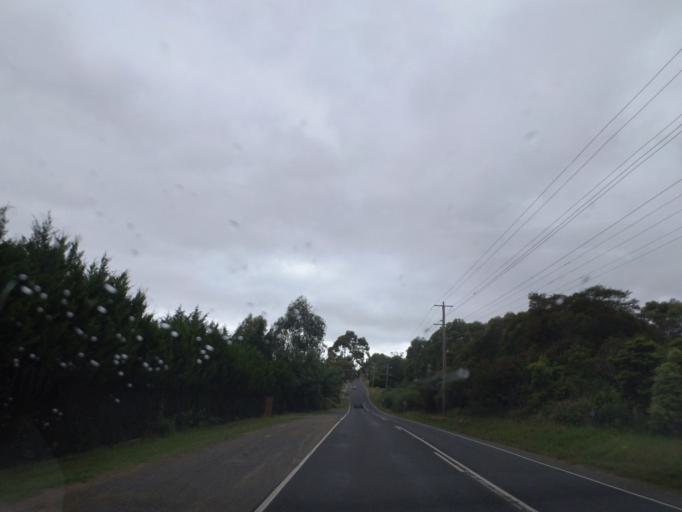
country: AU
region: Victoria
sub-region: Yarra Ranges
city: Mount Evelyn
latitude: -37.7823
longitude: 145.4187
